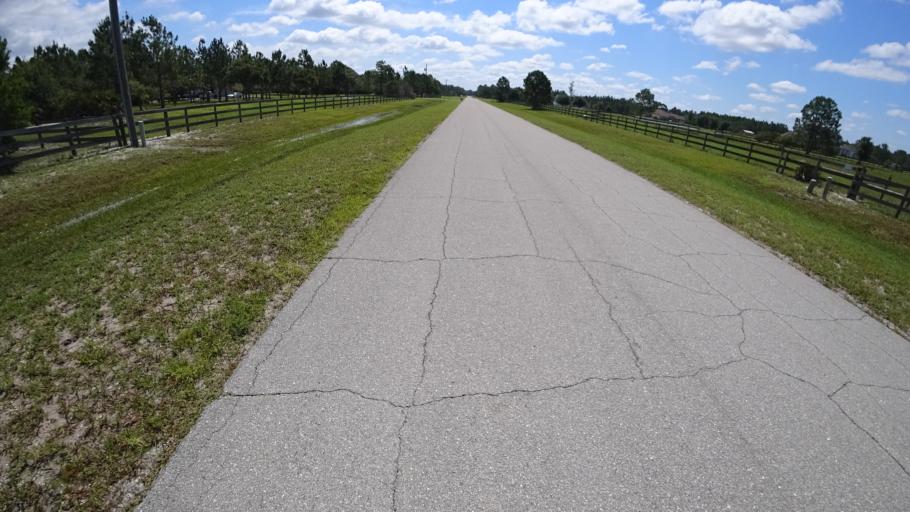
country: US
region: Florida
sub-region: Sarasota County
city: The Meadows
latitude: 27.4203
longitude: -82.3267
